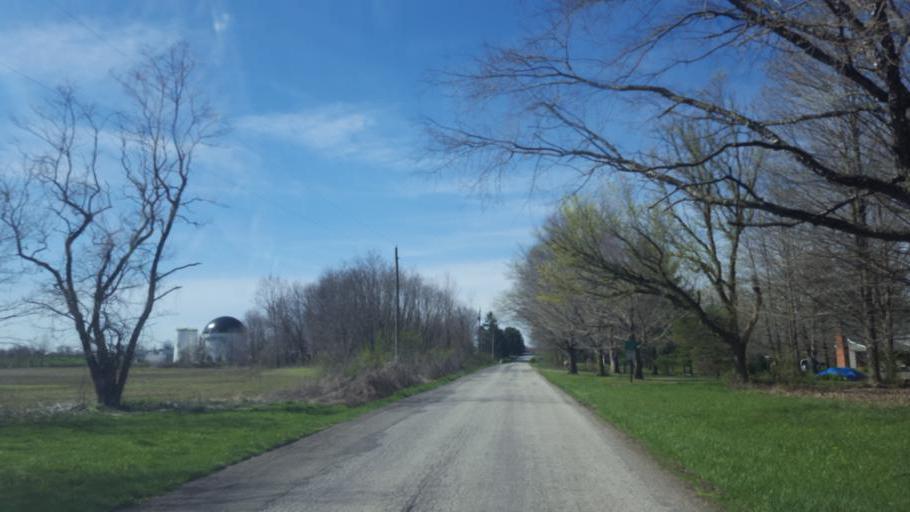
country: US
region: Ohio
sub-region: Delaware County
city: Ashley
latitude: 40.4481
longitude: -82.9604
